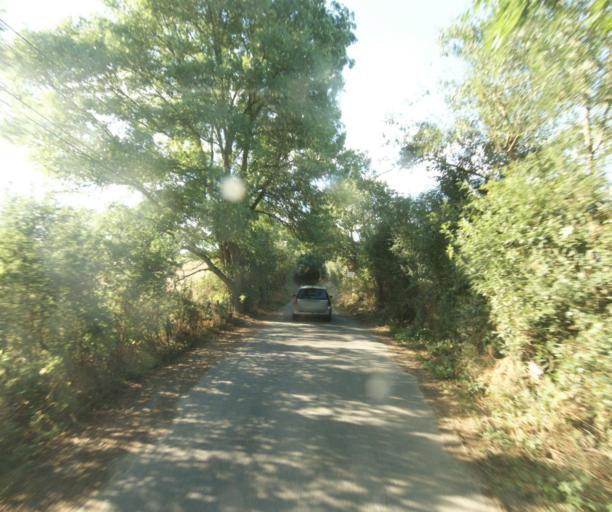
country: FR
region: Rhone-Alpes
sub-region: Departement du Rhone
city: Lozanne
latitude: 45.8481
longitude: 4.6869
